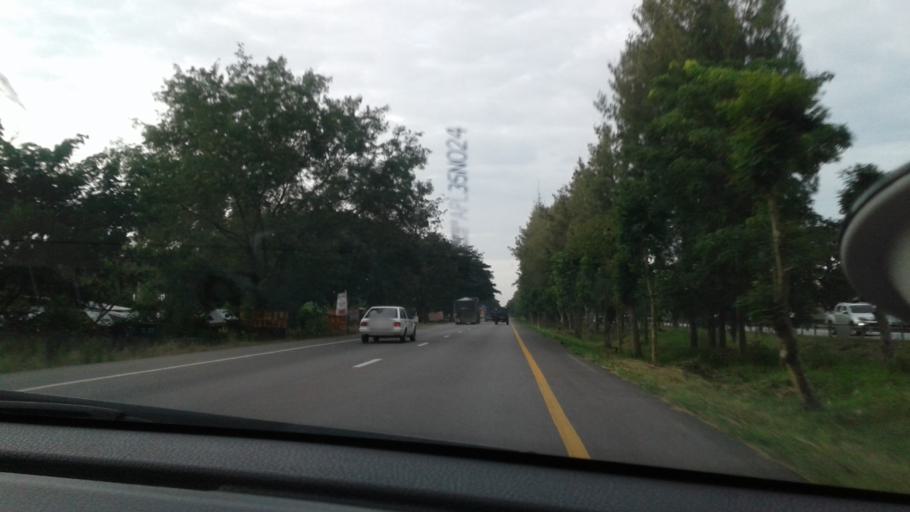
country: TH
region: Prachuap Khiri Khan
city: Pran Buri
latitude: 12.4325
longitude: 99.9144
